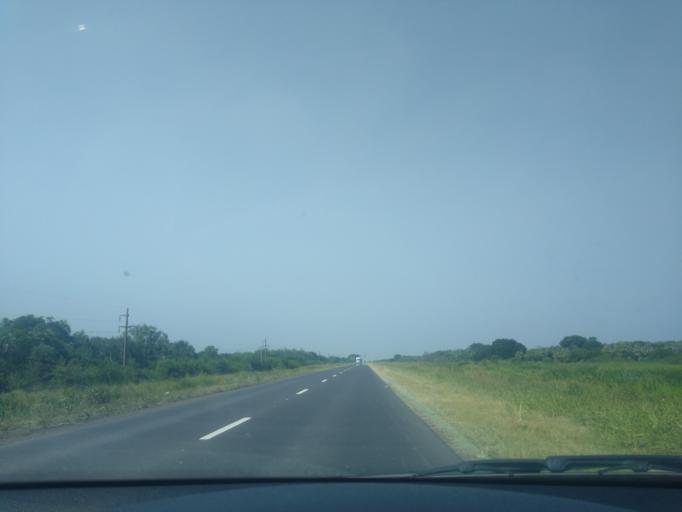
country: AR
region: Chaco
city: Fontana
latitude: -27.5501
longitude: -59.1398
